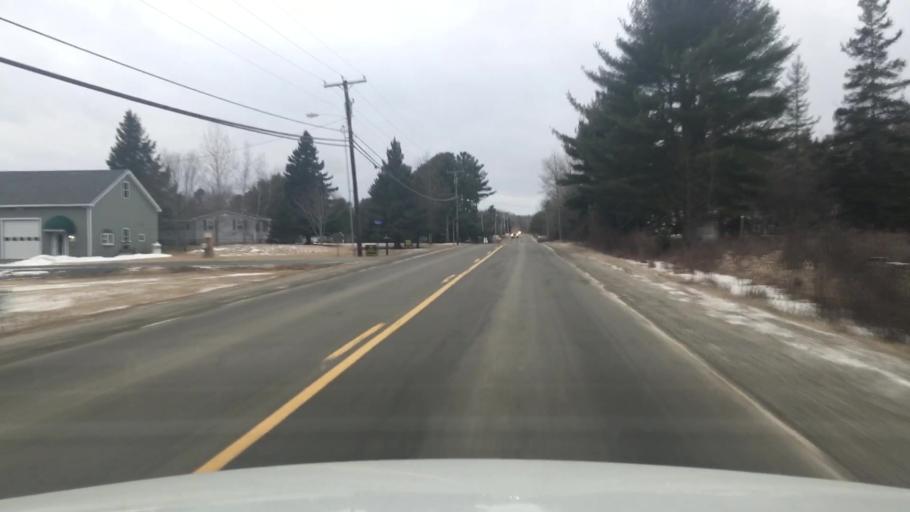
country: US
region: Maine
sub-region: Hancock County
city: Trenton
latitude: 44.5005
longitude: -68.3515
